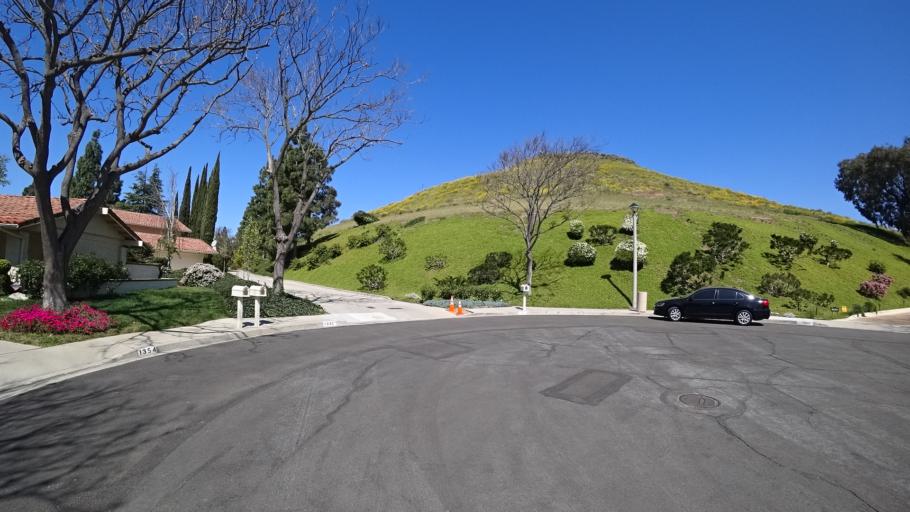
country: US
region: California
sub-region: Ventura County
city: Moorpark
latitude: 34.2319
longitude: -118.8557
